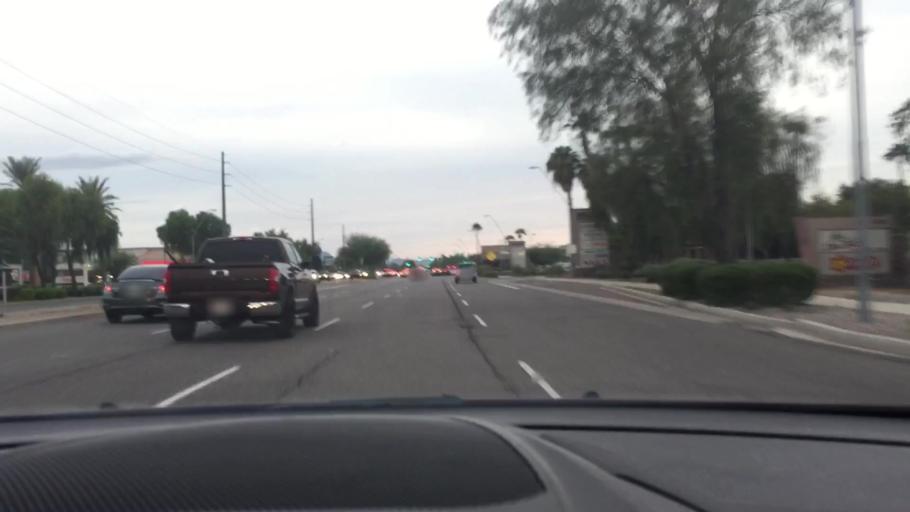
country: US
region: Arizona
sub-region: Maricopa County
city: Guadalupe
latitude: 33.3054
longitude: -111.9771
